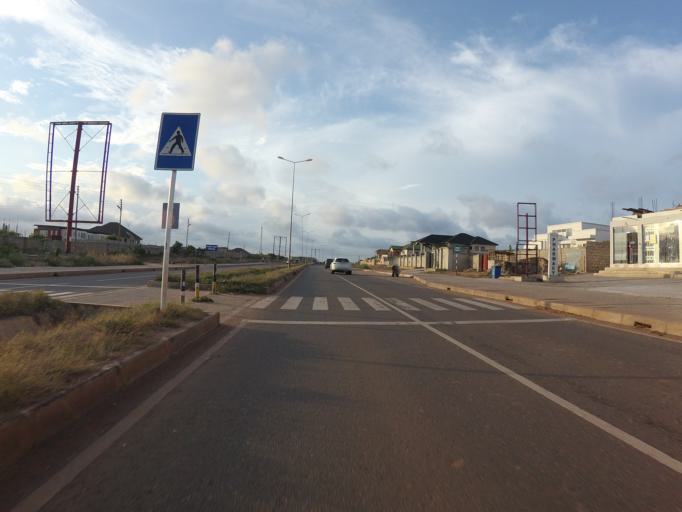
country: GH
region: Greater Accra
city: Teshi Old Town
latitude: 5.5996
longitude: -0.1363
